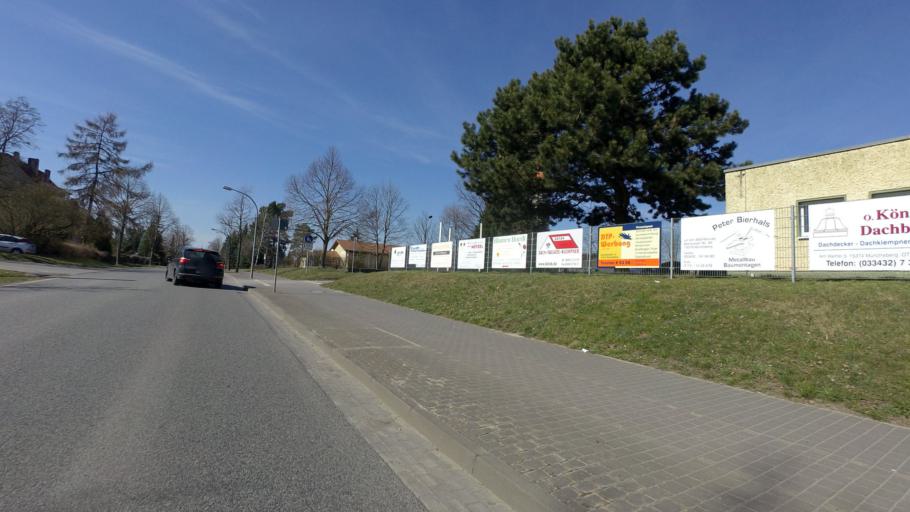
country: DE
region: Brandenburg
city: Muncheberg
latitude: 52.5069
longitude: 14.1337
